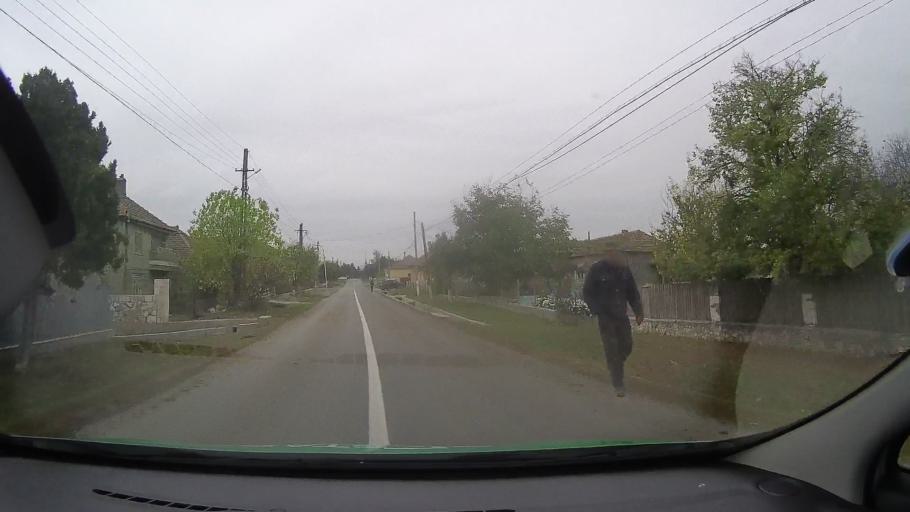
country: RO
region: Constanta
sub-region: Comuna Targusor
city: Targusor
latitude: 44.4630
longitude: 28.4201
